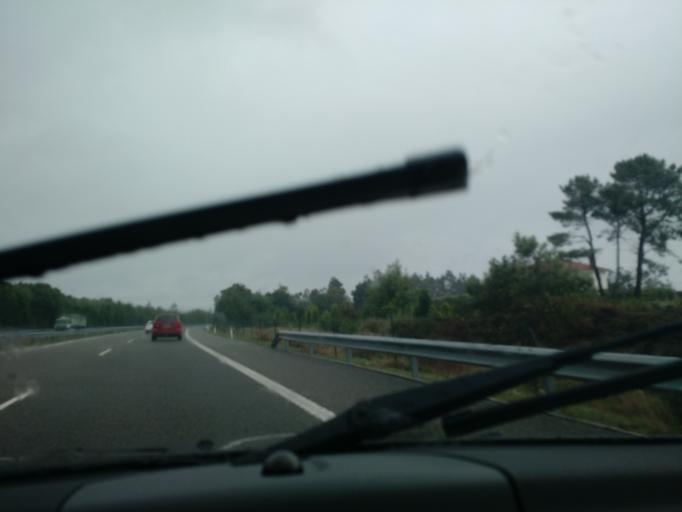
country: ES
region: Galicia
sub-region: Provincia da Coruna
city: Mesia
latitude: 43.1434
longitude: -8.3301
